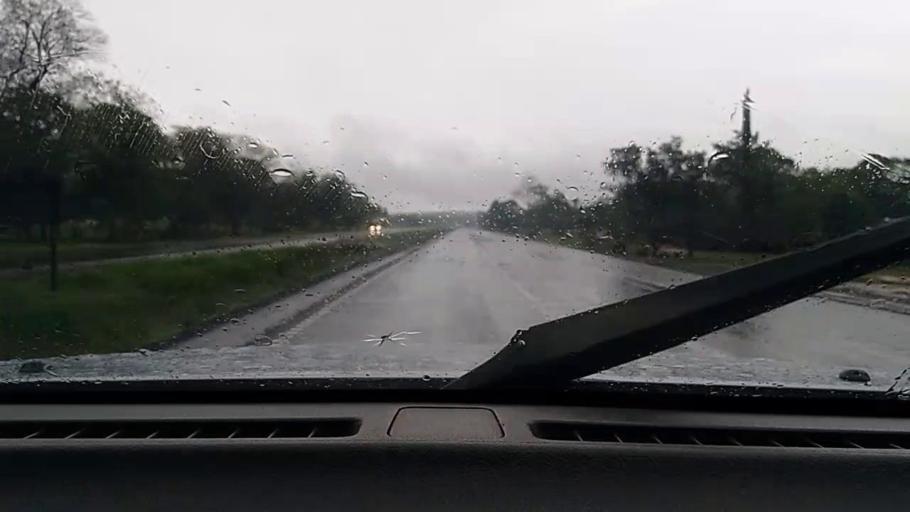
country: PY
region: Caaguazu
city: Repatriacion
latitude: -25.4617
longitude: -55.9257
